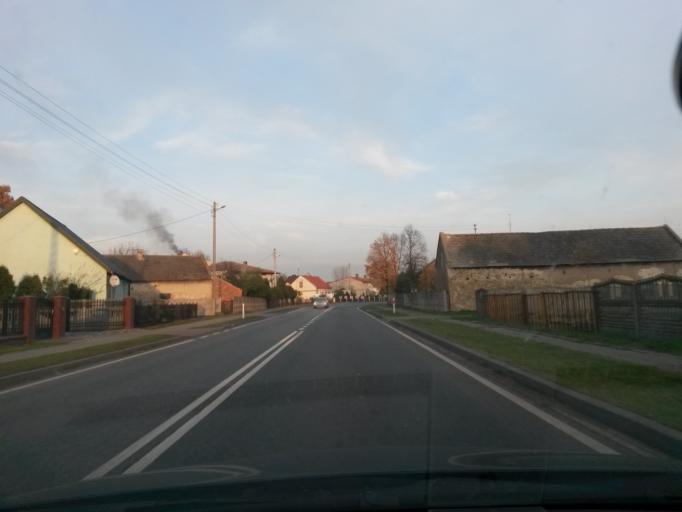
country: PL
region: Lodz Voivodeship
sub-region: Powiat wielunski
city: Wierzchlas
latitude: 51.2395
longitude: 18.6732
